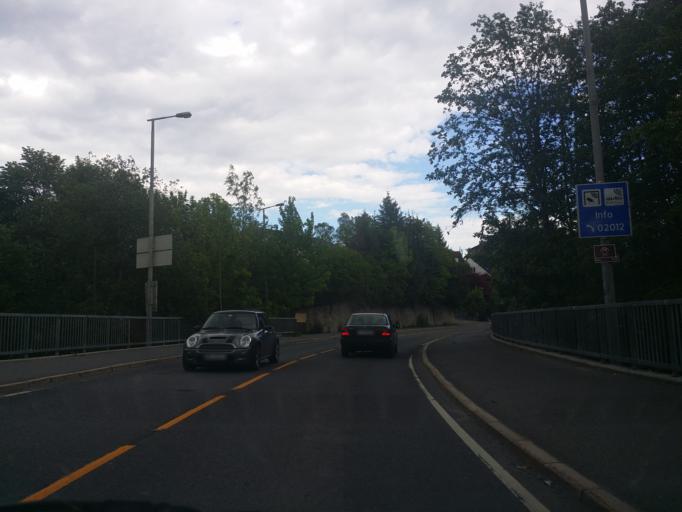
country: NO
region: Akershus
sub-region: Baerum
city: Lysaker
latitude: 59.9527
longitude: 10.6339
